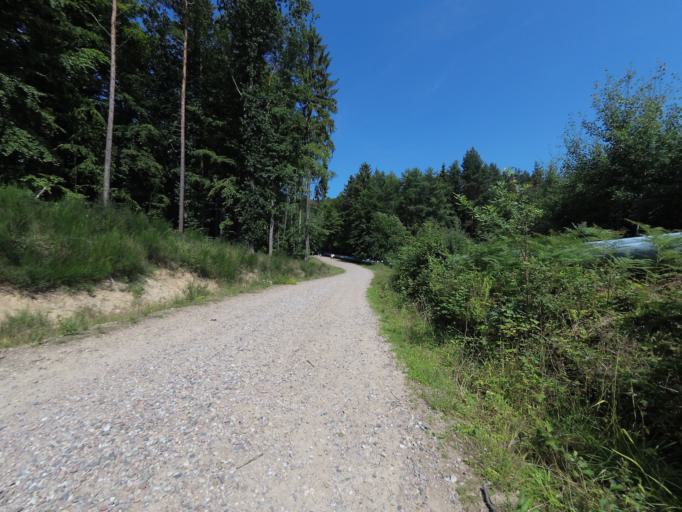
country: PL
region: Pomeranian Voivodeship
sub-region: Gdynia
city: Wielki Kack
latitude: 54.4864
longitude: 18.5016
